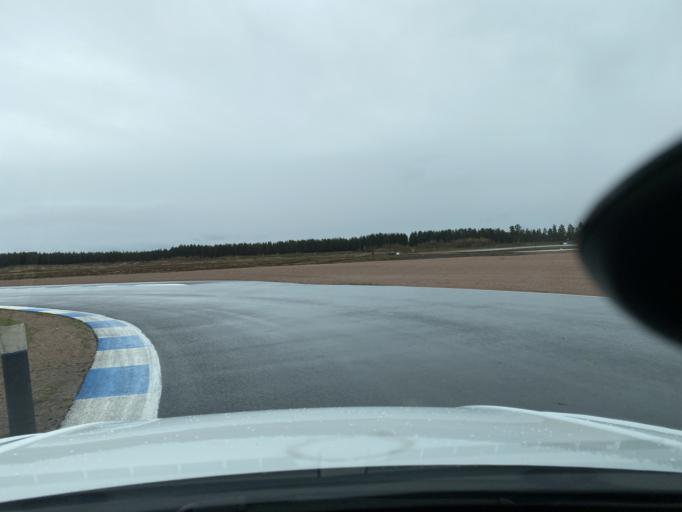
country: FI
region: Satakunta
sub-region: Pori
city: Vampula
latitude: 60.9778
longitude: 22.6605
